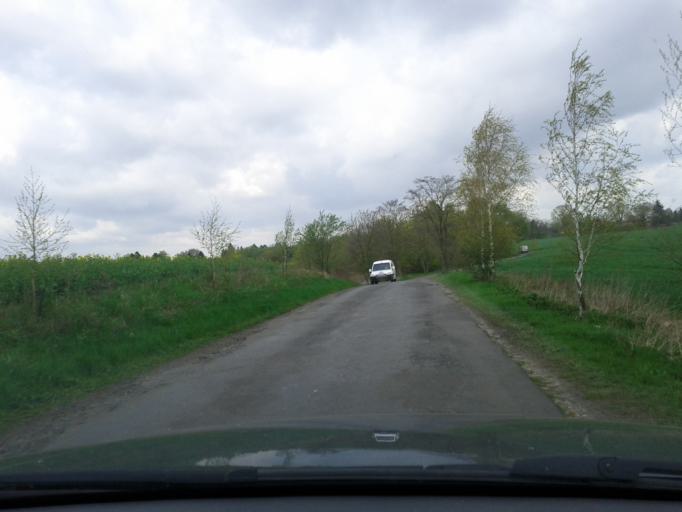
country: DE
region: Brandenburg
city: Schoneiche
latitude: 52.4844
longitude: 13.6788
